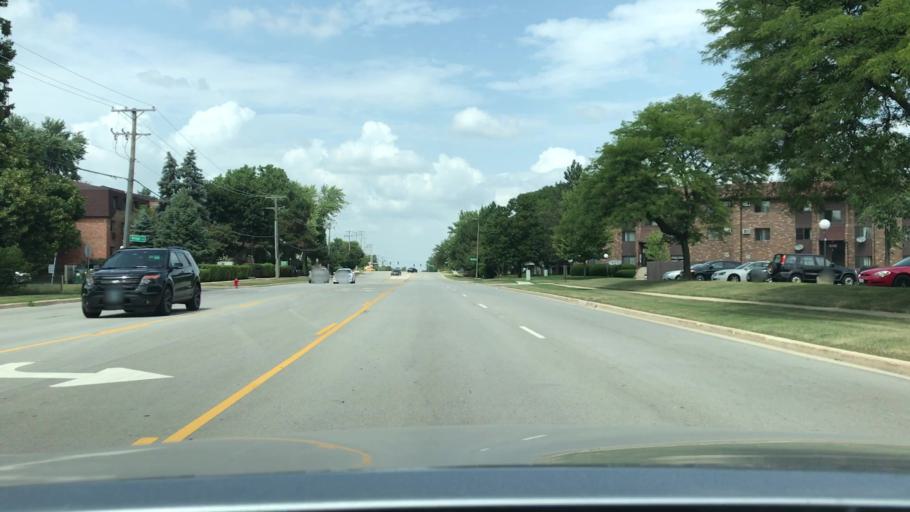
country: US
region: Illinois
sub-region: DuPage County
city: Woodridge
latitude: 41.7468
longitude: -88.0309
